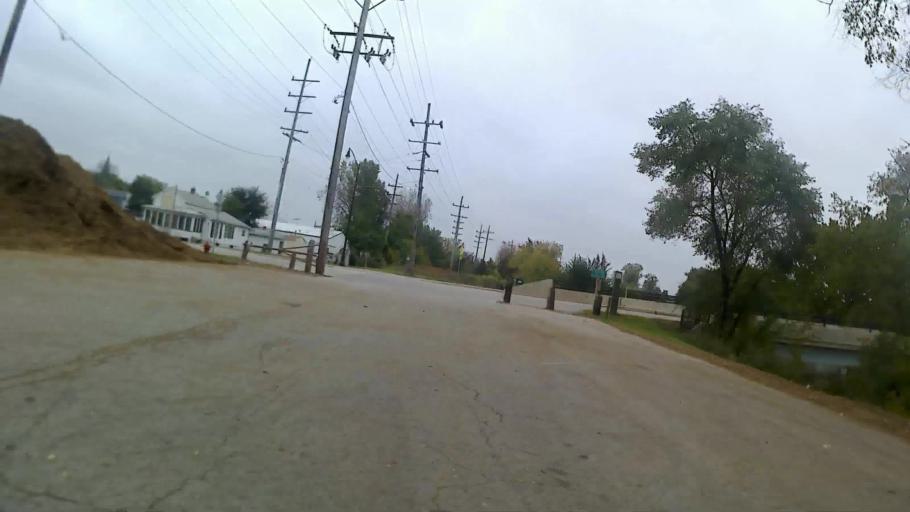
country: US
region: Illinois
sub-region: Kane County
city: Aurora
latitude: 41.7711
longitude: -88.3079
